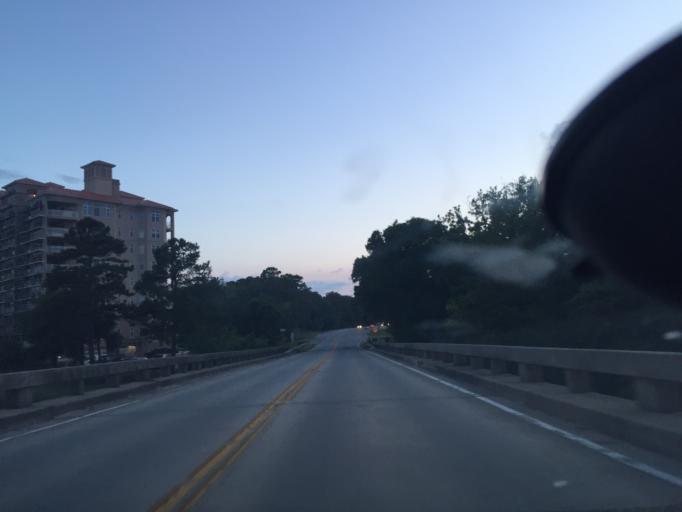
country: US
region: Georgia
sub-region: Chatham County
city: Wilmington Island
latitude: 32.0349
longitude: -80.9599
